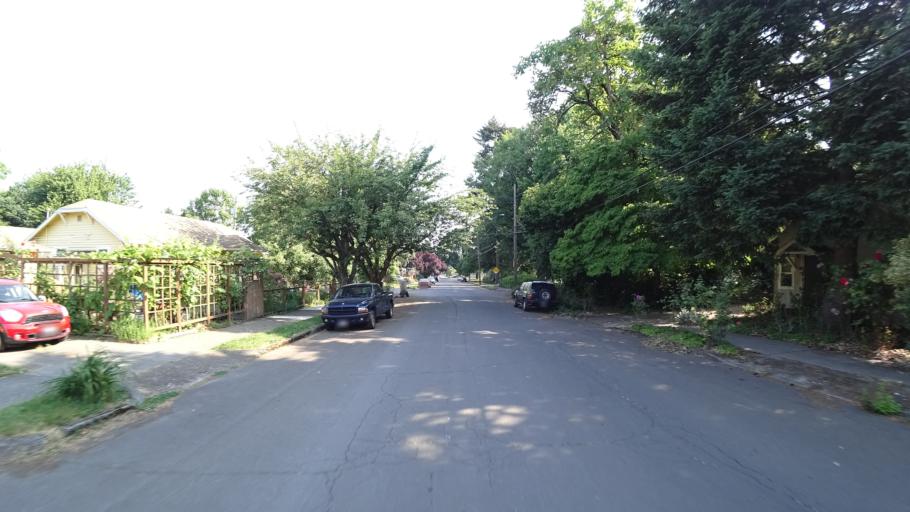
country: US
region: Oregon
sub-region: Washington County
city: West Haven
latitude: 45.5928
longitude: -122.7402
